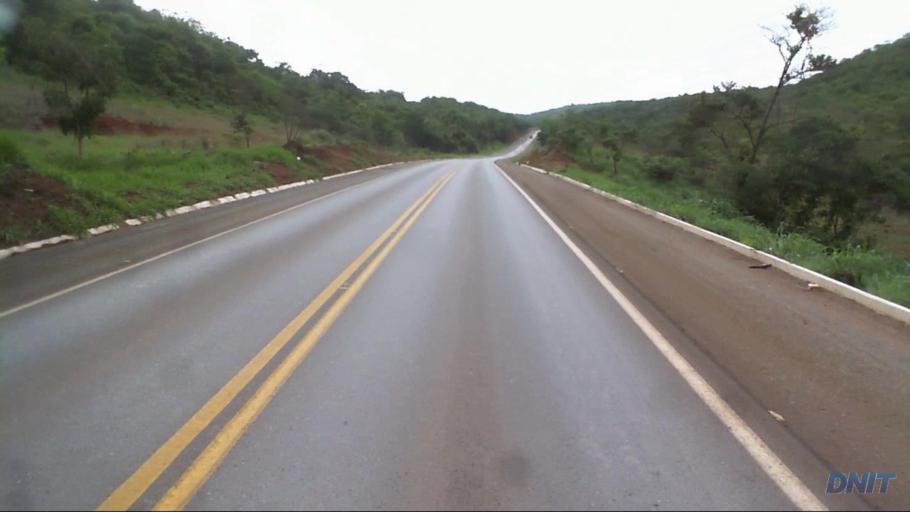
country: BR
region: Goias
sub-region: Barro Alto
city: Barro Alto
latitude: -14.9187
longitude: -48.9520
